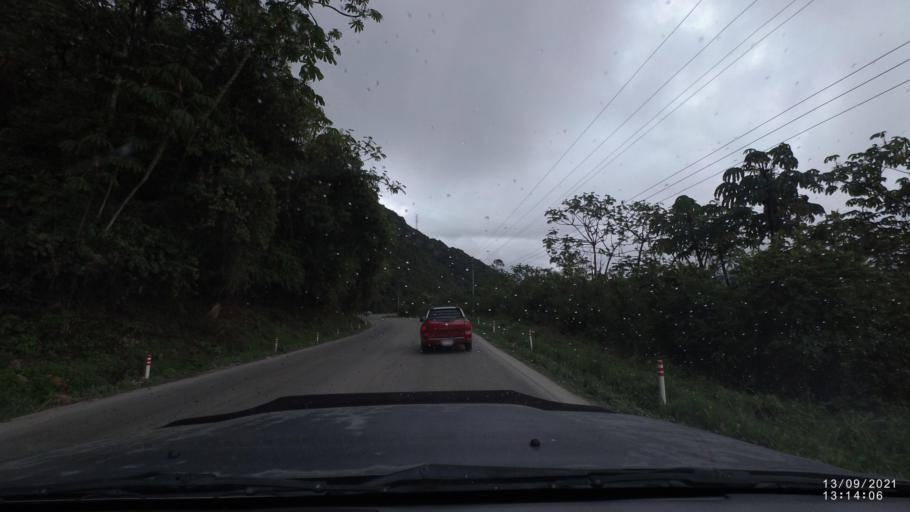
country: BO
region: Cochabamba
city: Colomi
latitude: -17.1976
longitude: -65.8473
